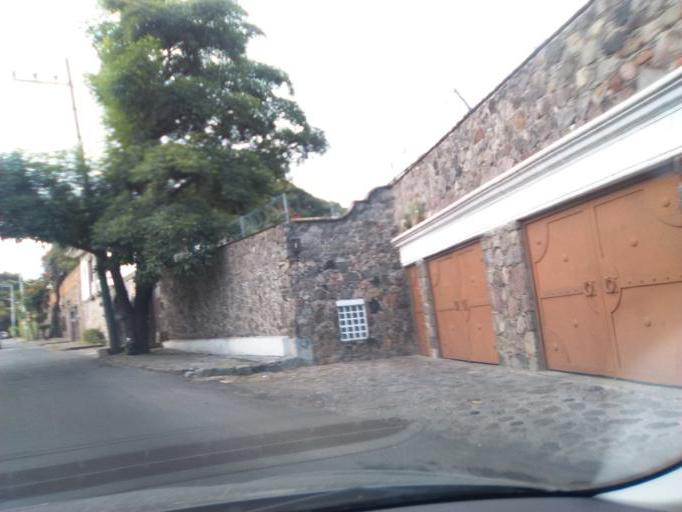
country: MX
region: Morelos
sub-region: Cuernavaca
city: Cuernavaca
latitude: 18.9022
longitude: -99.2260
